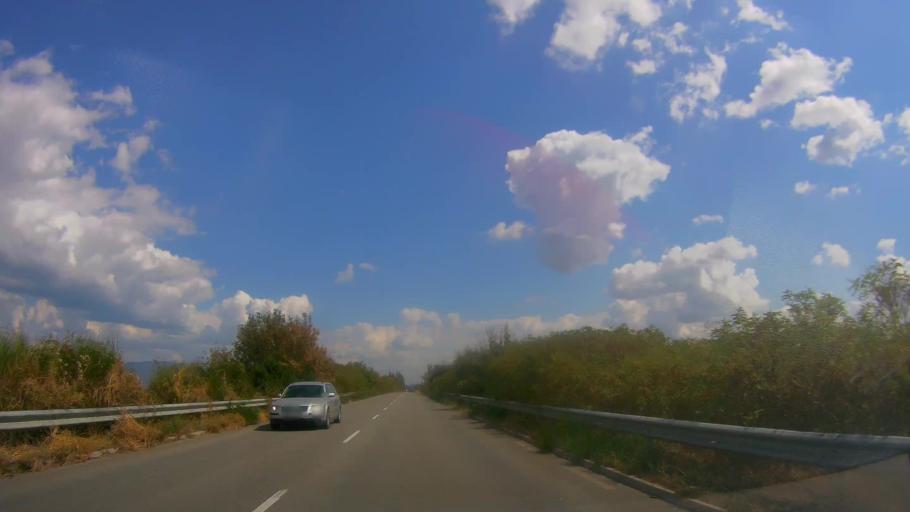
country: BG
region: Sliven
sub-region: Obshtina Tvurditsa
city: Tvurditsa
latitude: 42.6560
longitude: 25.9326
